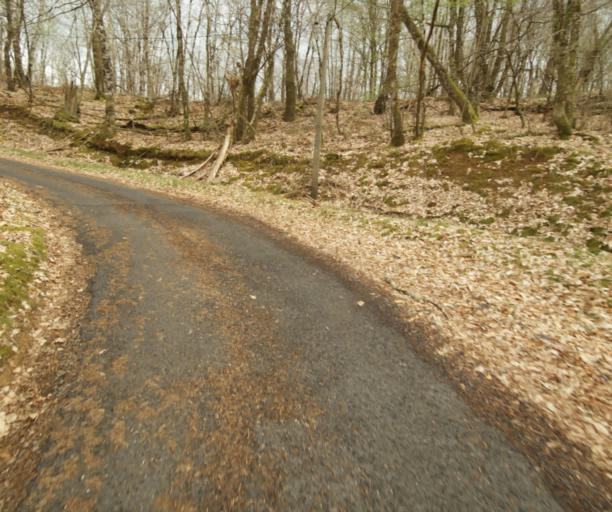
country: FR
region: Limousin
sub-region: Departement de la Correze
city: Naves
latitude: 45.3150
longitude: 1.8131
